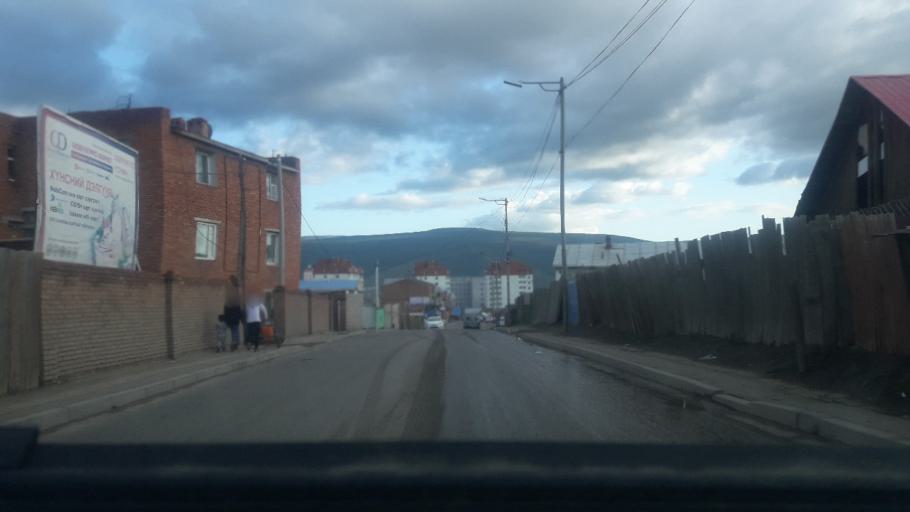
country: MN
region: Ulaanbaatar
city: Ulaanbaatar
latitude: 47.9208
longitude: 106.9954
